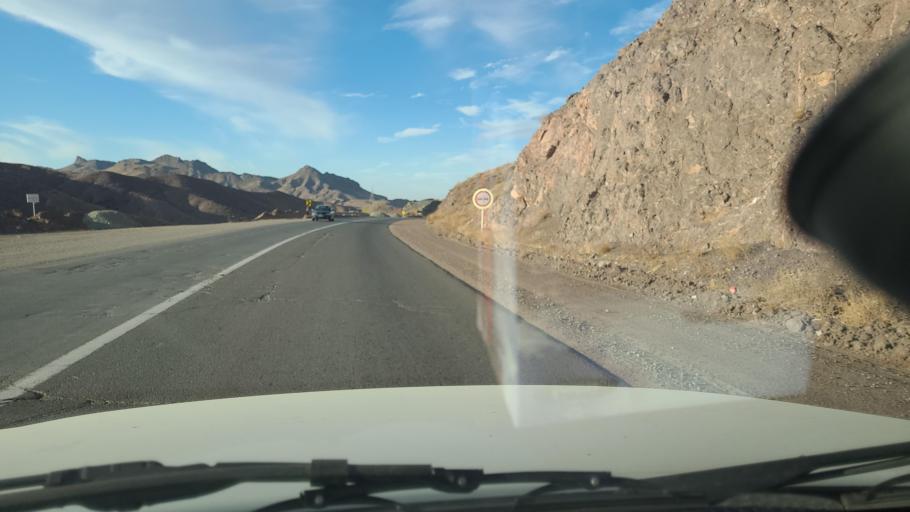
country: IR
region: Razavi Khorasan
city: Sabzevar
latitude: 36.4231
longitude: 57.5643
